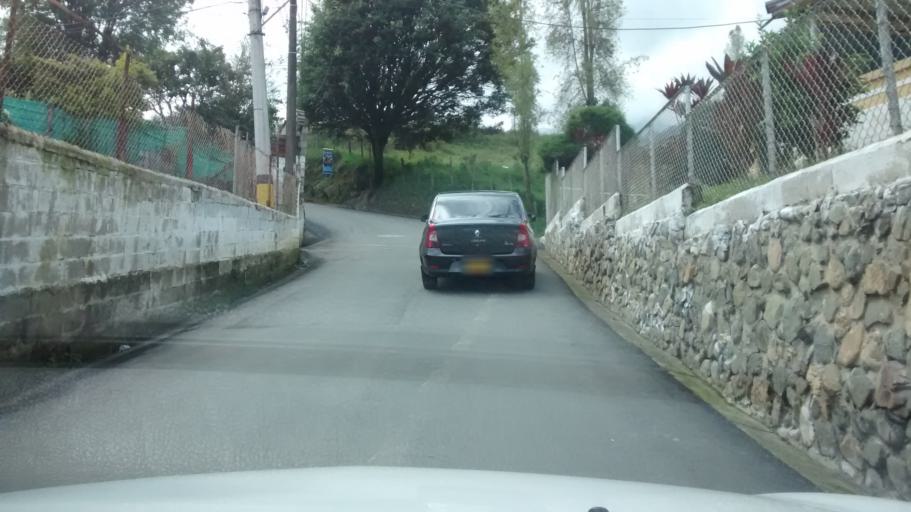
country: CO
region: Antioquia
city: La Estrella
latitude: 6.1768
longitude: -75.6608
